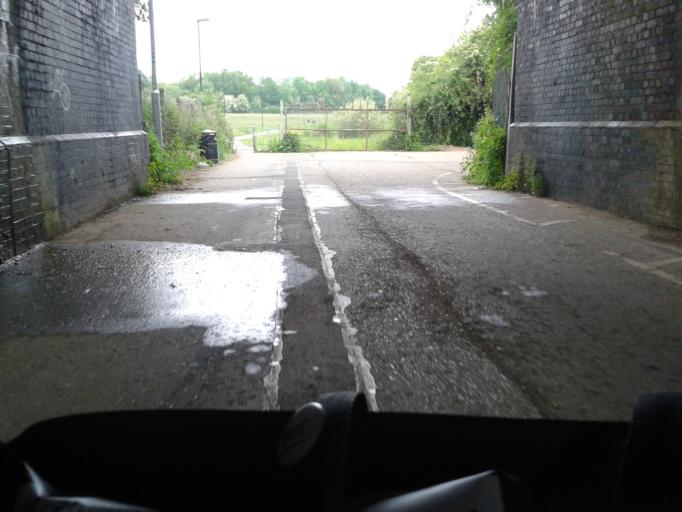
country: GB
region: England
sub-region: Cambridgeshire
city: Huntingdon
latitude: 52.3331
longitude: -0.1911
